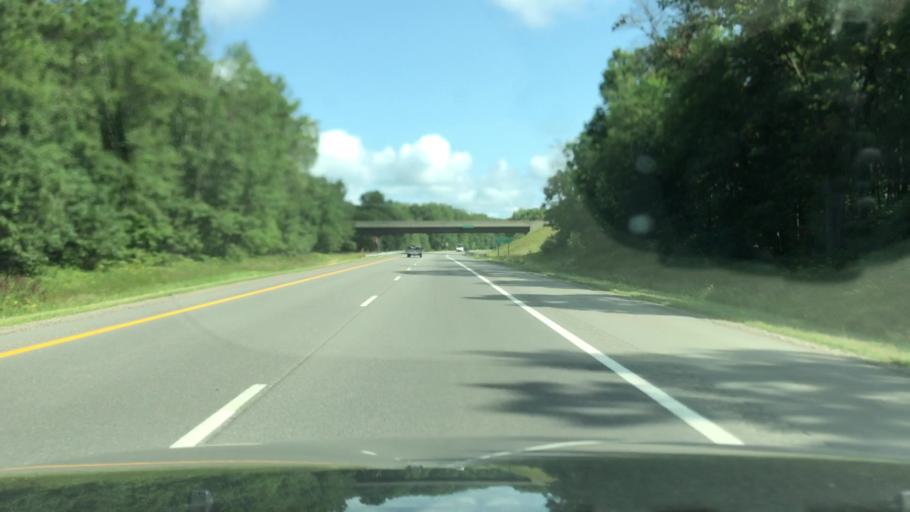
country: US
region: Michigan
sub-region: Montcalm County
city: Howard City
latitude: 43.4374
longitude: -85.4926
